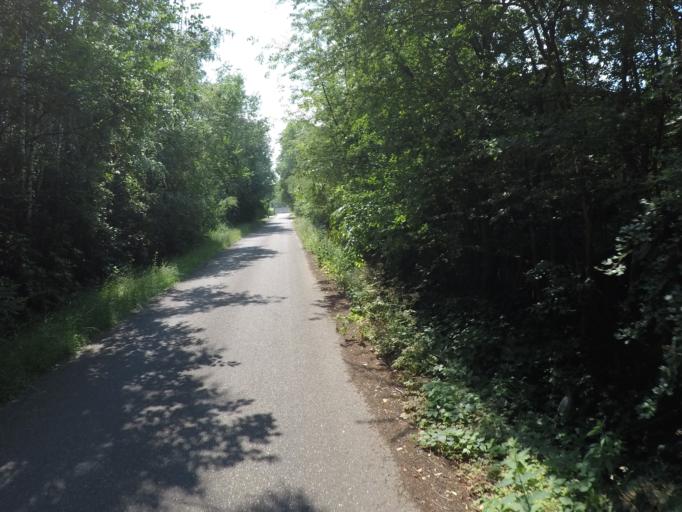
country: BE
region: Flanders
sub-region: Provincie Antwerpen
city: Rijkevorsel
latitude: 51.3364
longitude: 4.7261
